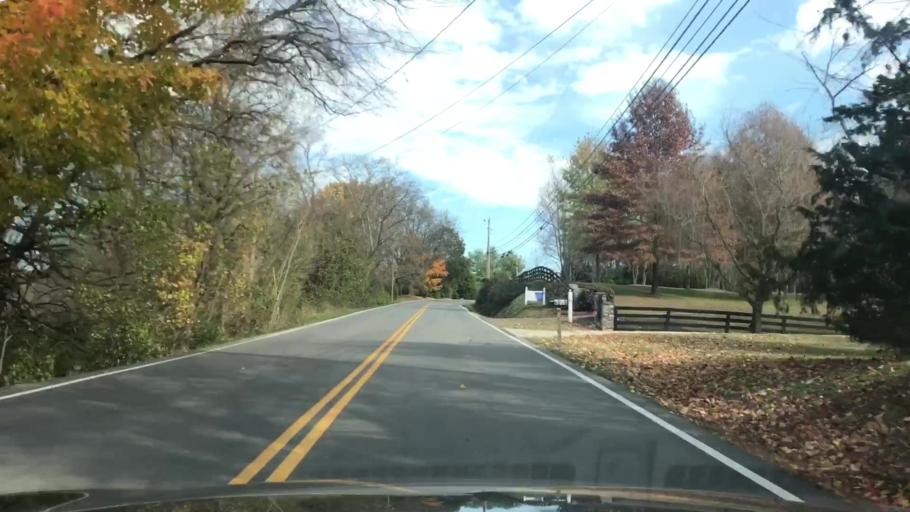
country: US
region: Tennessee
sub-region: Williamson County
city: Franklin
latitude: 35.9169
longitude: -86.7977
